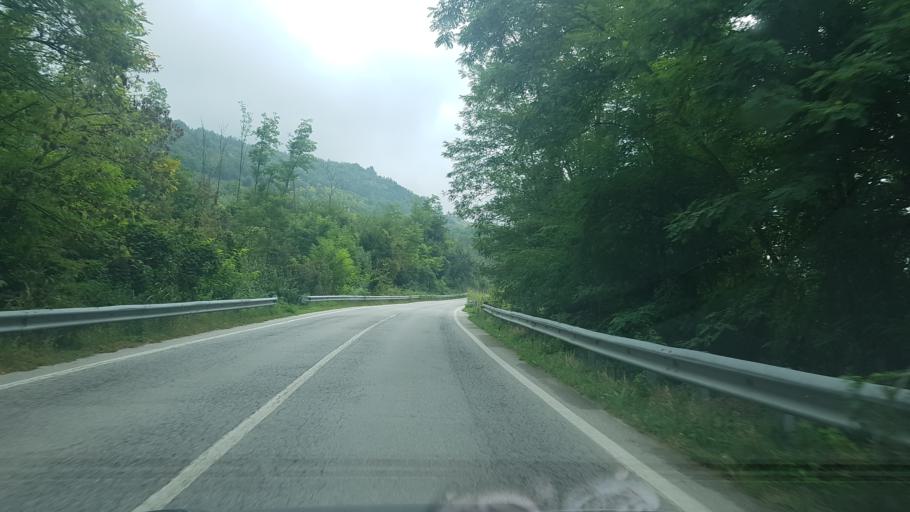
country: IT
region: Piedmont
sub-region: Provincia di Cuneo
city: Bastia Mondovi
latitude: 44.4407
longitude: 7.8991
